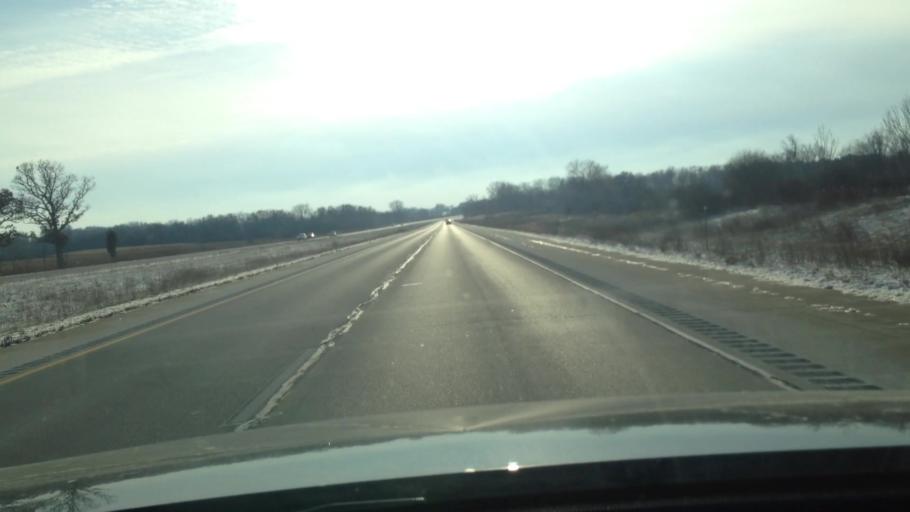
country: US
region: Wisconsin
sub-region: Walworth County
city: Potter Lake
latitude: 42.8157
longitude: -88.3637
